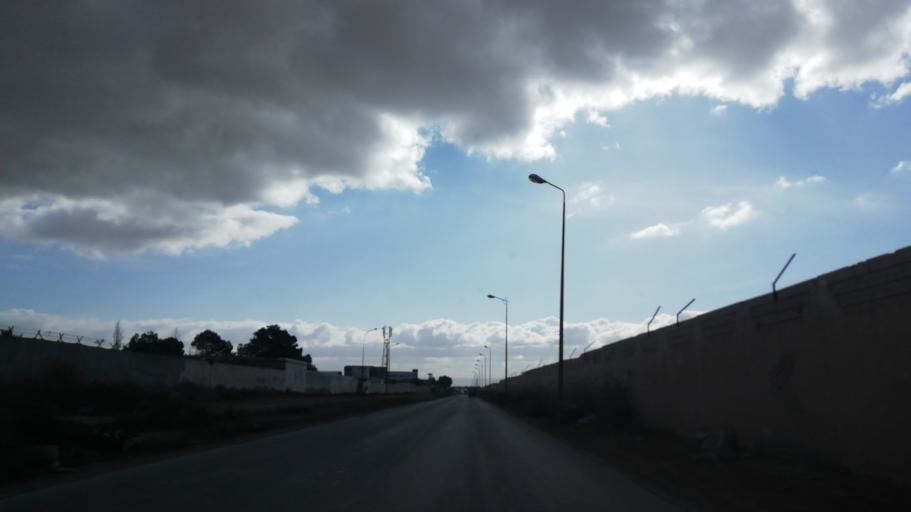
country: DZ
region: Oran
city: Es Senia
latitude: 35.6307
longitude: -0.5939
